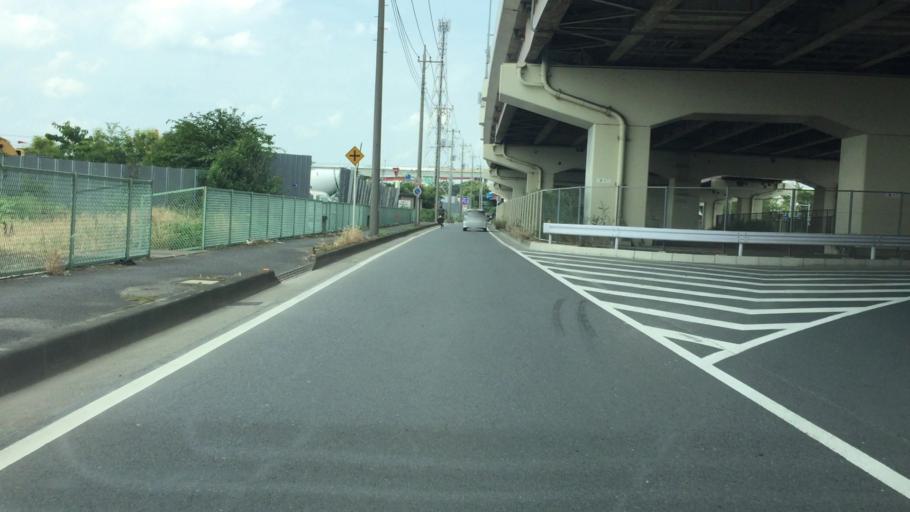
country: JP
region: Saitama
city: Yashio-shi
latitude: 35.8323
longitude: 139.8557
